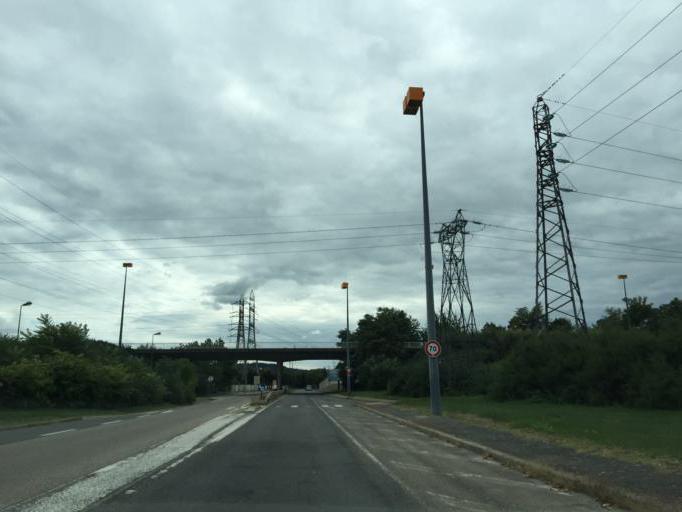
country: FR
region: Rhone-Alpes
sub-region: Departement de la Loire
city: La Talaudiere
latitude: 45.4638
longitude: 4.4106
